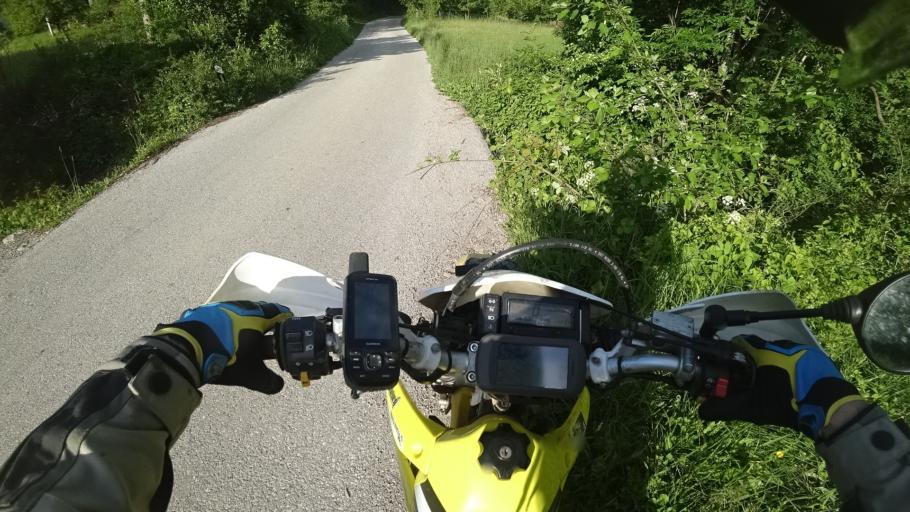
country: HR
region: Licko-Senjska
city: Gospic
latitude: 44.4913
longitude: 15.3048
